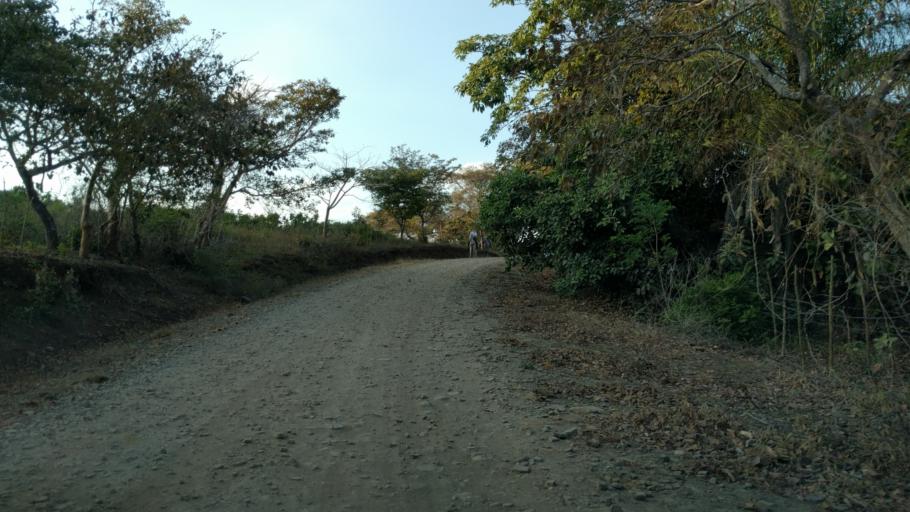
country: CR
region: Puntarenas
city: Esparza
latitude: 10.0253
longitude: -84.6987
